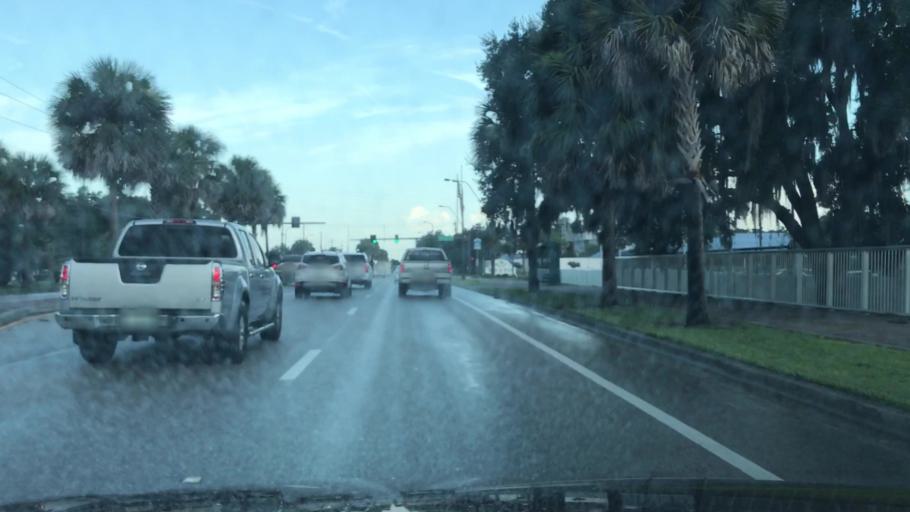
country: US
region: Florida
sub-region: Sarasota County
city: Fruitville
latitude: 27.3384
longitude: -82.4258
